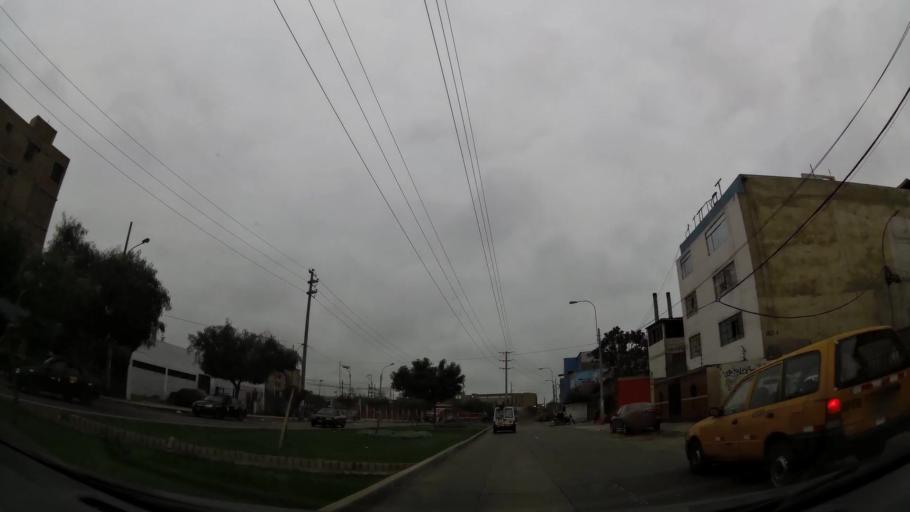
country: PE
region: Lima
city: Lima
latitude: -12.0603
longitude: -77.0632
